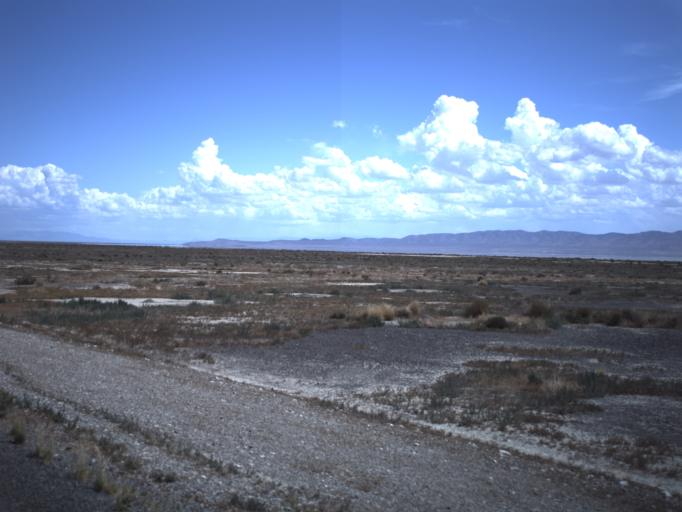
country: US
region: Utah
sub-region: Millard County
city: Delta
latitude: 39.0935
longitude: -113.1663
